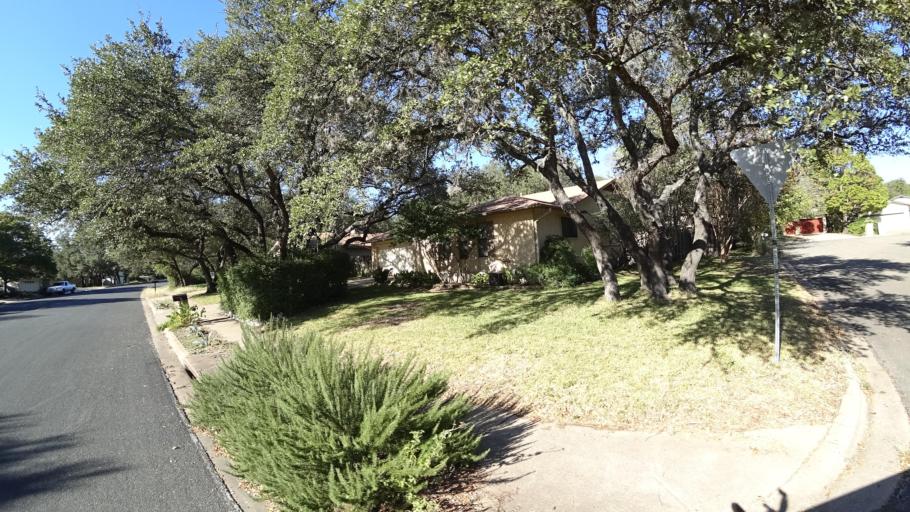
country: US
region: Texas
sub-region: Williamson County
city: Jollyville
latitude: 30.4225
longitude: -97.7728
